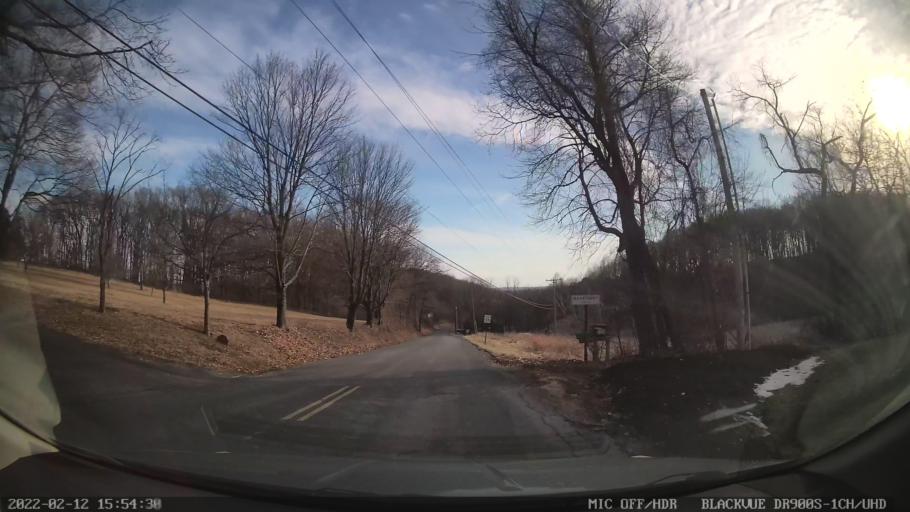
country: US
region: Pennsylvania
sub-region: Berks County
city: Kutztown
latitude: 40.5707
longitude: -75.7517
